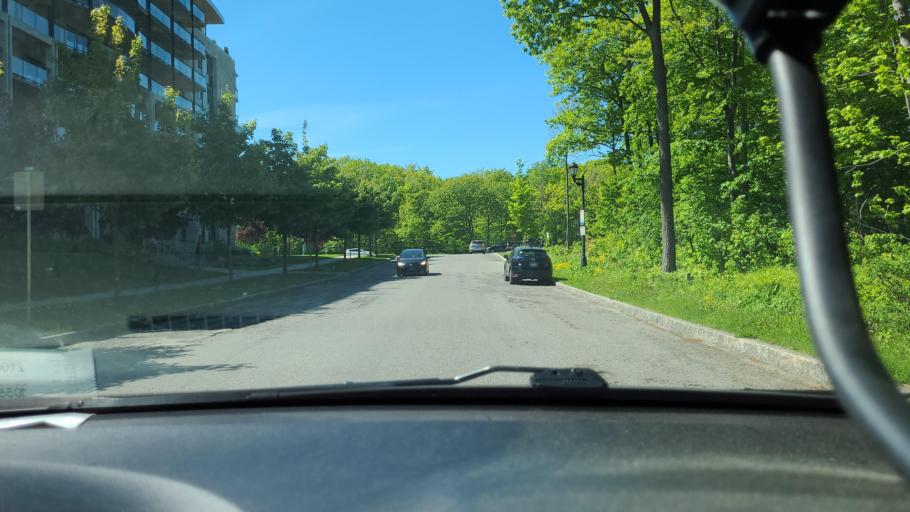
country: CA
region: Quebec
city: L'Ancienne-Lorette
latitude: 46.7559
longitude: -71.3260
